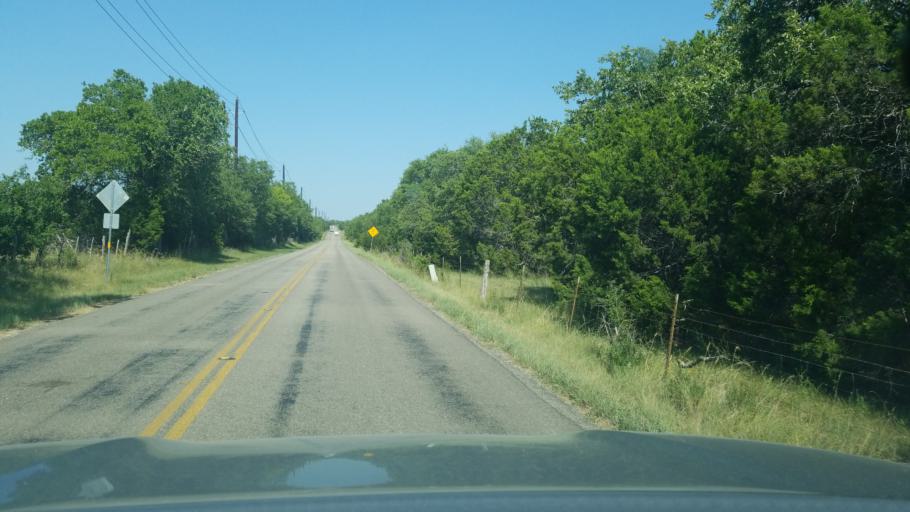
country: US
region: Texas
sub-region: Comal County
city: Bulverde
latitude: 29.7692
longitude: -98.5241
